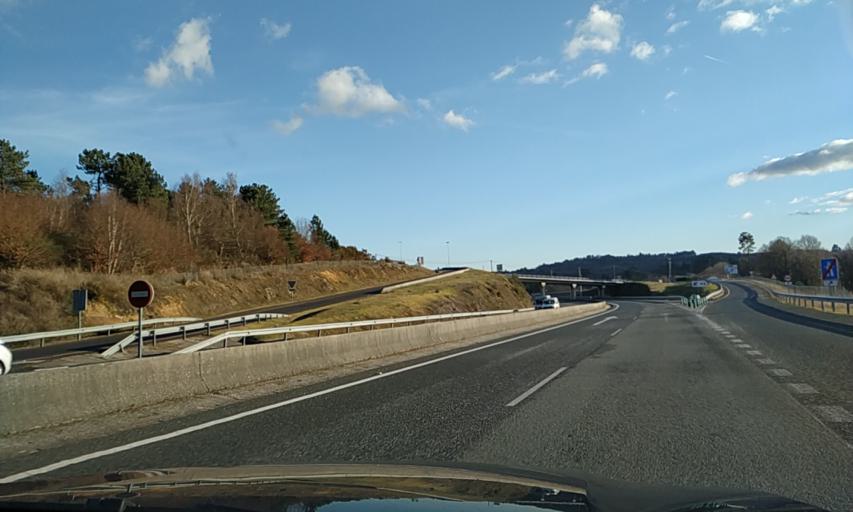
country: ES
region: Galicia
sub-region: Provincia de Pontevedra
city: Lalin
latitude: 42.6410
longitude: -8.1325
